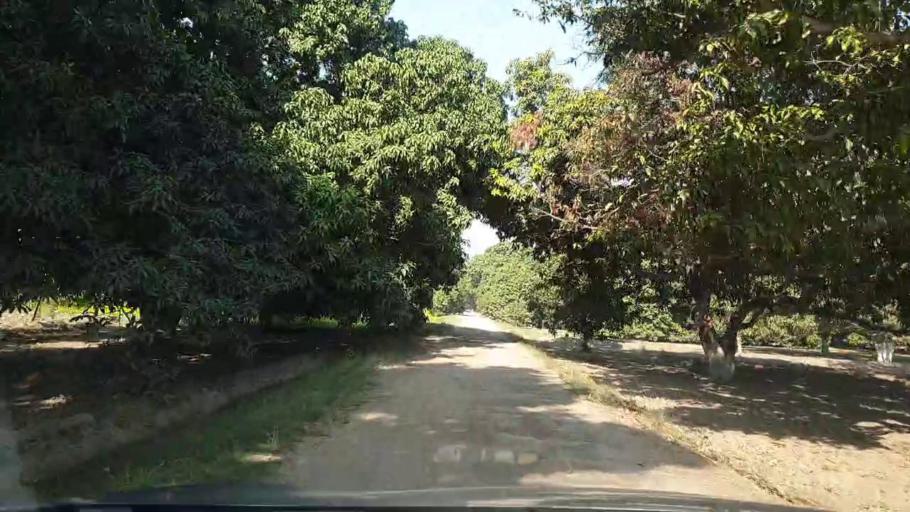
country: PK
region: Sindh
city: Tando Allahyar
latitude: 25.4663
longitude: 68.6278
